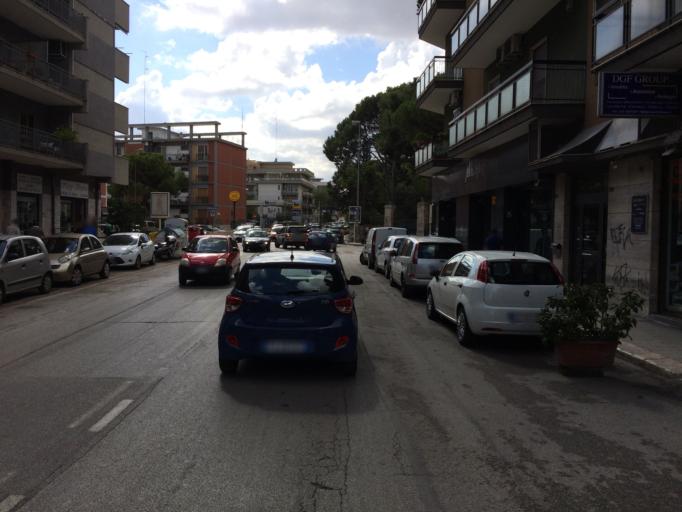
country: IT
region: Apulia
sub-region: Provincia di Bari
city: Bari
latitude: 41.1034
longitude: 16.8790
